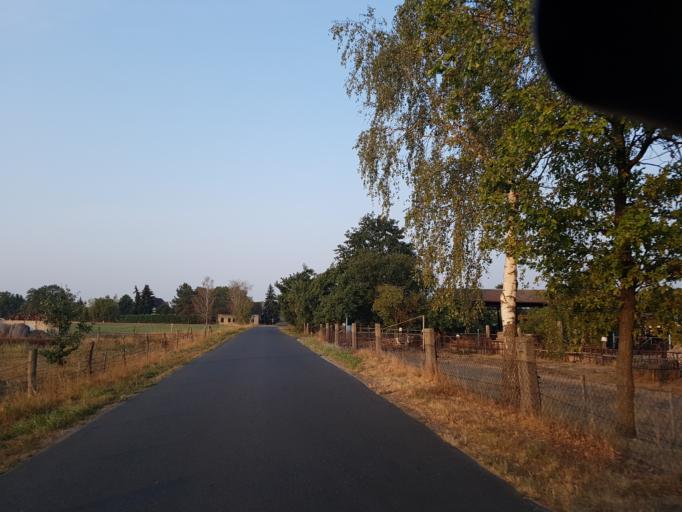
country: DE
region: Brandenburg
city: Falkenberg
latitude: 51.5412
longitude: 13.2852
